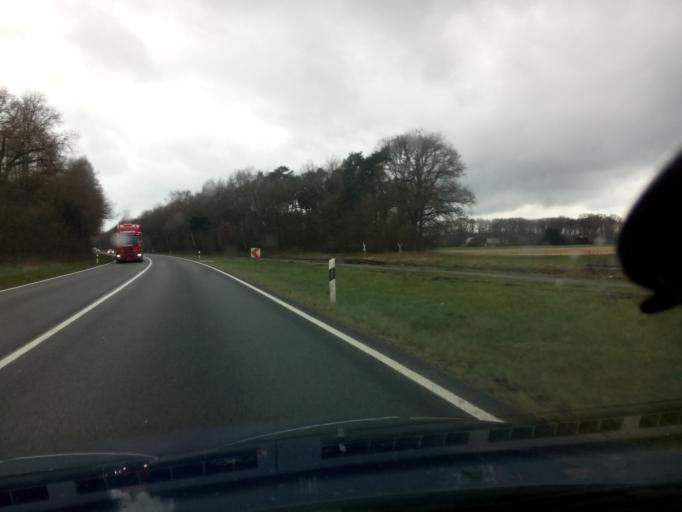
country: DE
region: Lower Saxony
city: Herzlake
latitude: 52.6941
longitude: 7.5532
